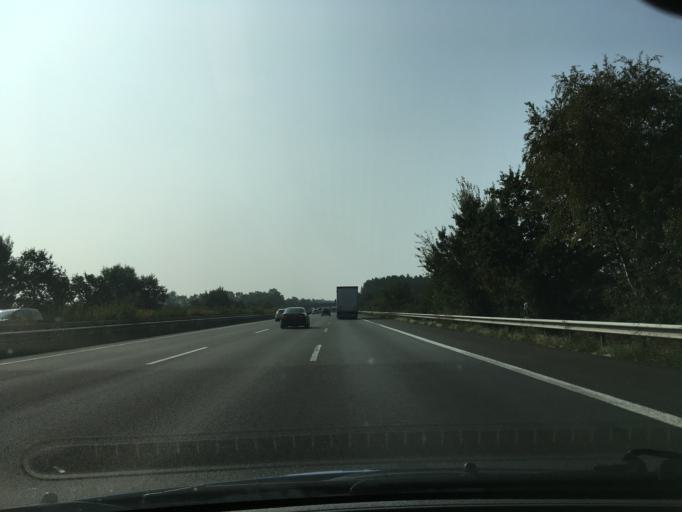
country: DE
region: Lower Saxony
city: Essel
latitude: 52.7202
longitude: 9.6808
